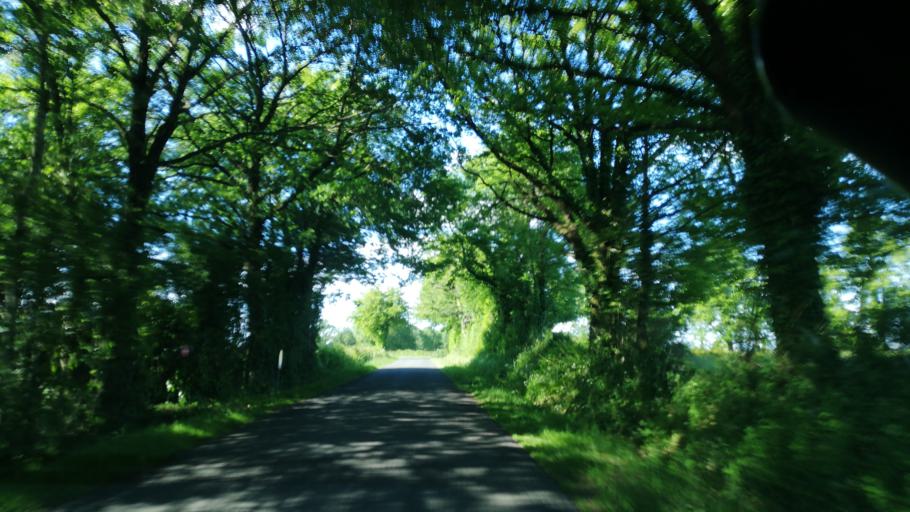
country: FR
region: Poitou-Charentes
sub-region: Departement des Deux-Sevres
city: Moncoutant
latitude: 46.6728
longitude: -0.5699
